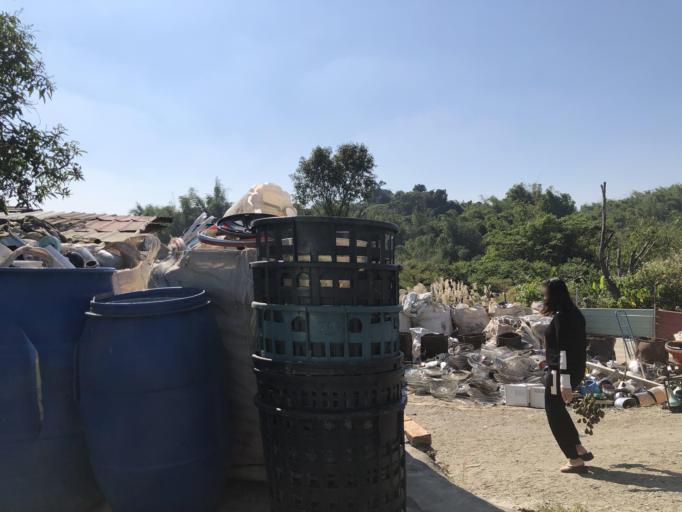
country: TW
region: Taiwan
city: Yujing
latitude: 23.0477
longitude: 120.3761
